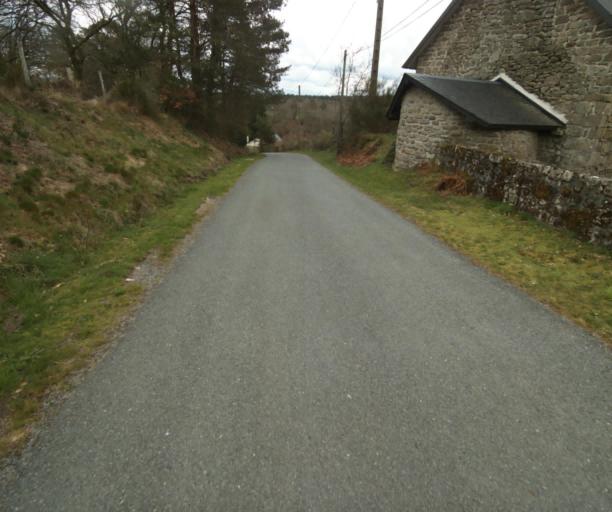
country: FR
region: Limousin
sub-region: Departement de la Correze
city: Correze
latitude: 45.3154
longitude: 1.8824
